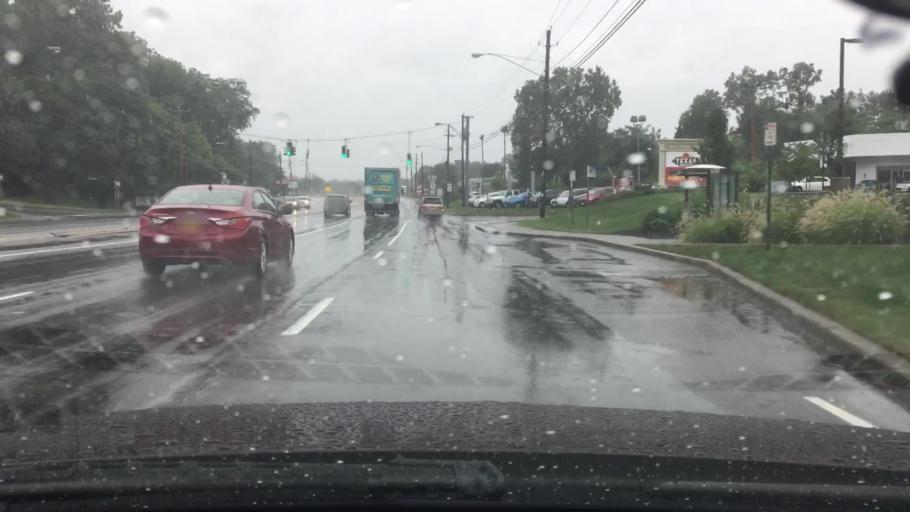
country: US
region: New York
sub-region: Dutchess County
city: Spackenkill
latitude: 41.6477
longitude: -73.9255
